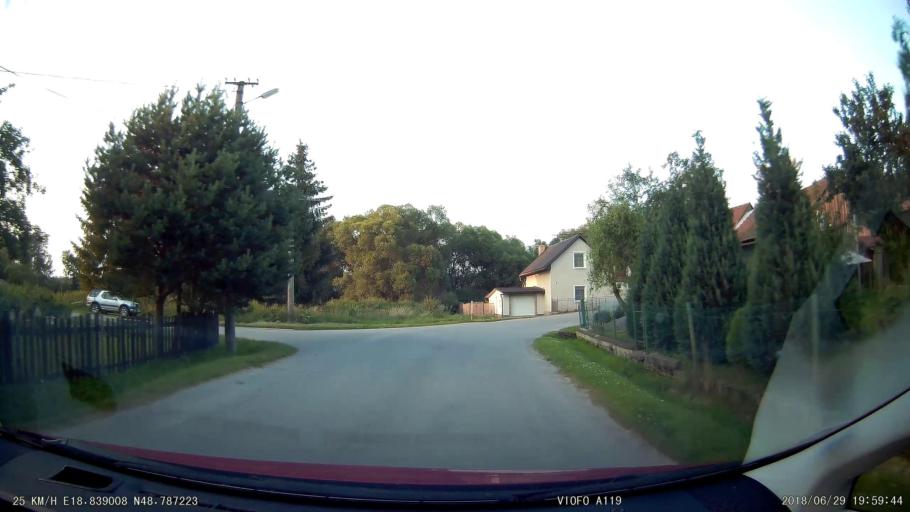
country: SK
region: Nitriansky
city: Handlova
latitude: 48.7873
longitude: 18.8391
